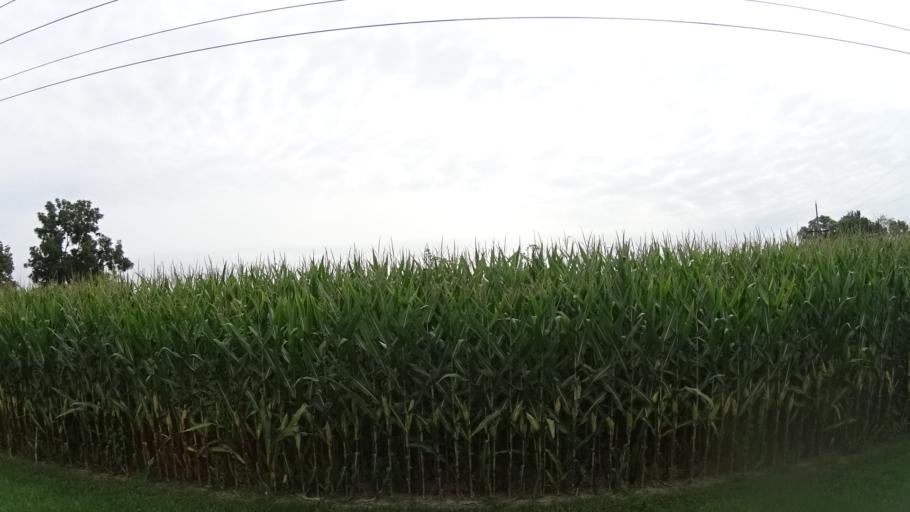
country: US
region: Indiana
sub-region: Madison County
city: Pendleton
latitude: 40.0080
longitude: -85.7870
